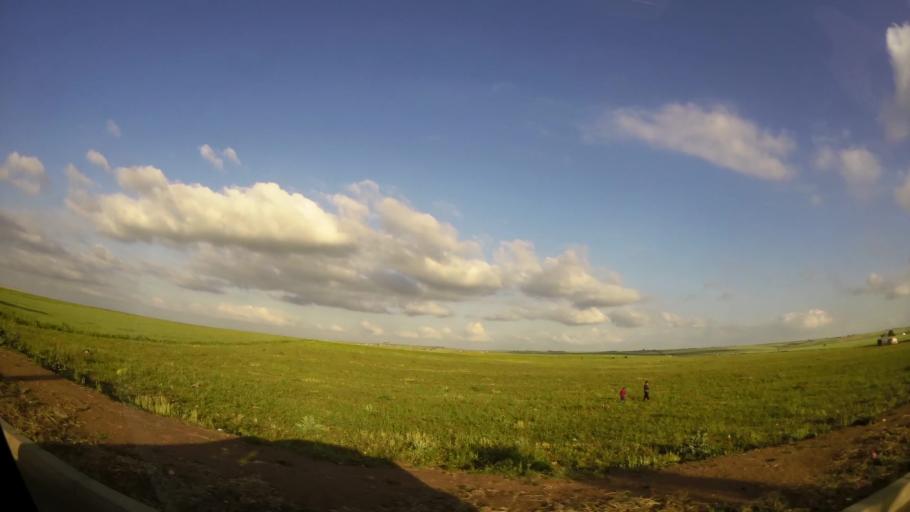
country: MA
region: Chaouia-Ouardigha
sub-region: Settat Province
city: Settat
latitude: 33.0038
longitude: -7.5960
